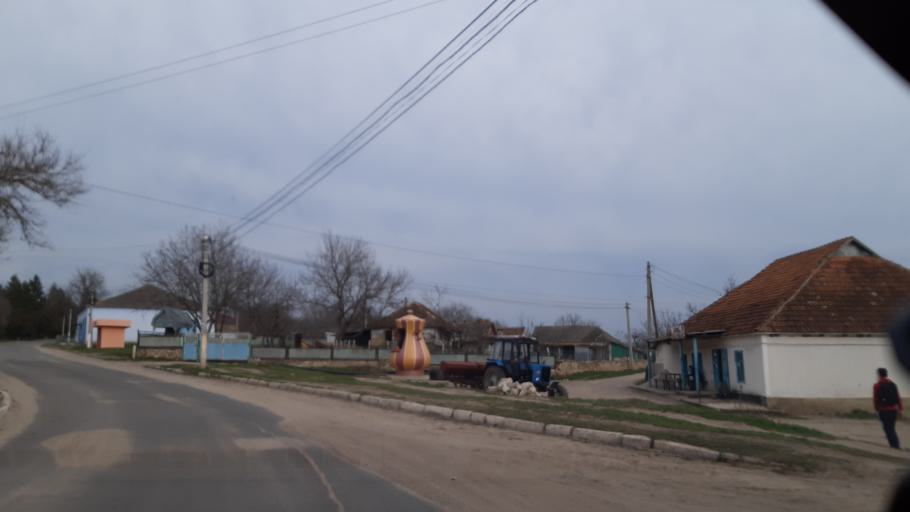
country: MD
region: Soldanesti
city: Soldanesti
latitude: 47.6838
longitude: 28.7596
